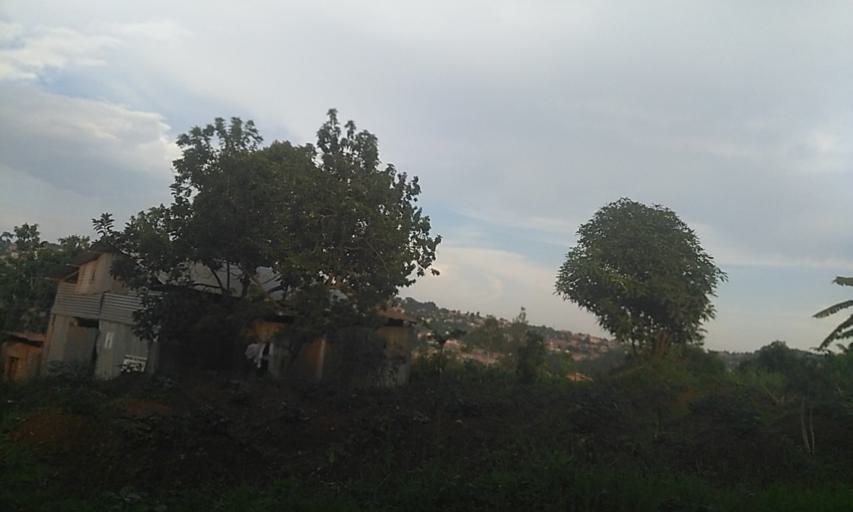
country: UG
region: Central Region
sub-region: Wakiso District
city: Kajansi
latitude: 0.2645
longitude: 32.5296
